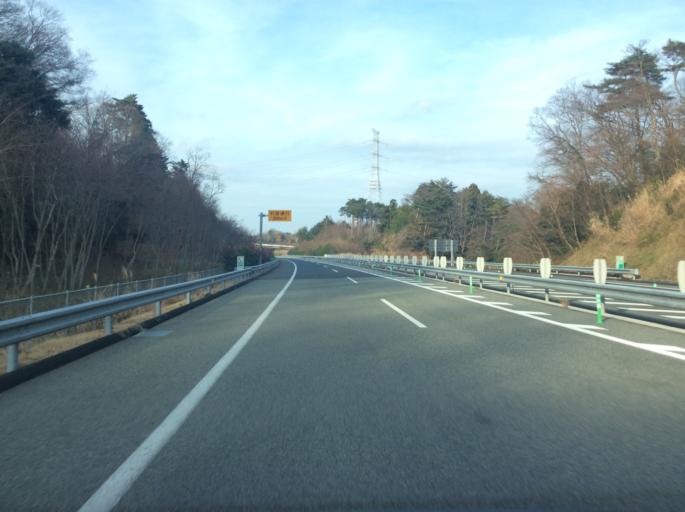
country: JP
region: Fukushima
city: Namie
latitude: 37.3128
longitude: 140.9926
